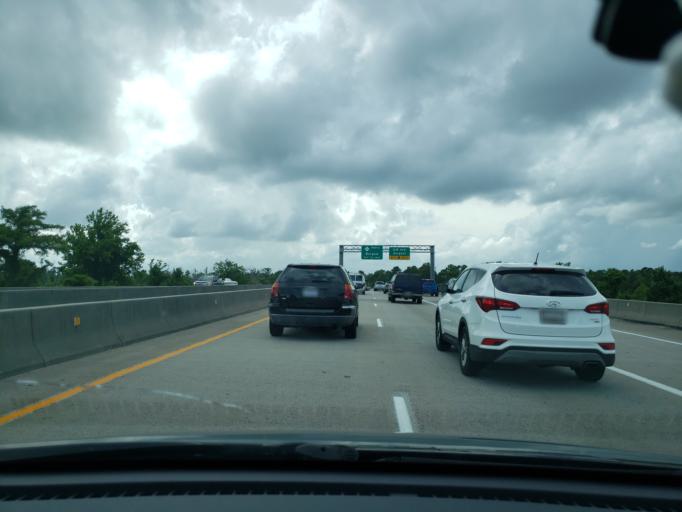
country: US
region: North Carolina
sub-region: New Hanover County
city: Wrightsboro
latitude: 34.2585
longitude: -77.9196
